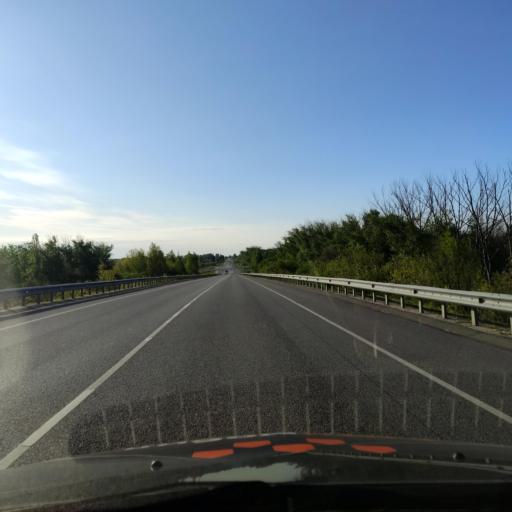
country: RU
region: Lipetsk
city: Yelets
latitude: 52.5632
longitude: 38.6807
